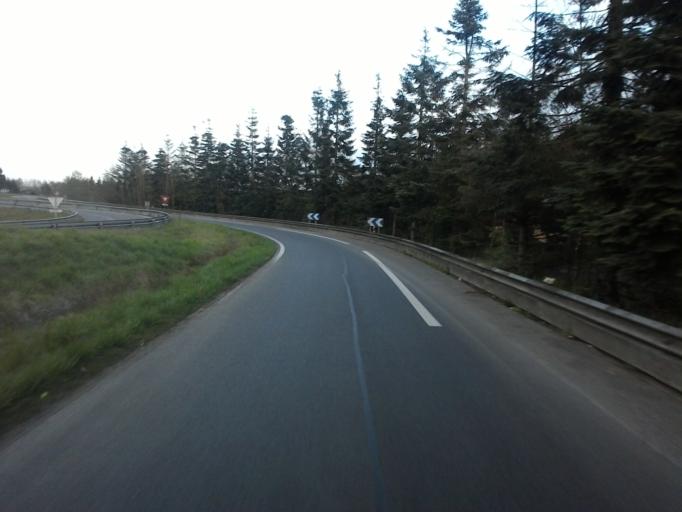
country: FR
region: Champagne-Ardenne
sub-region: Departement des Ardennes
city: Donchery
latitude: 49.6936
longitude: 4.9046
